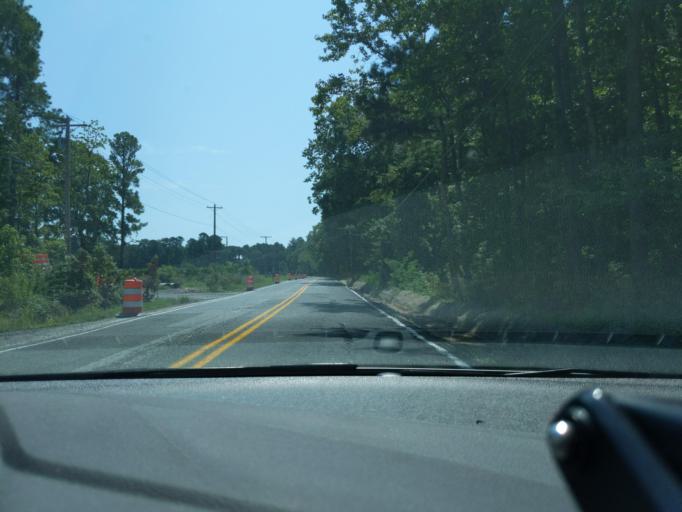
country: US
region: Virginia
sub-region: Northumberland County
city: Heathsville
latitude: 38.0759
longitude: -76.3468
